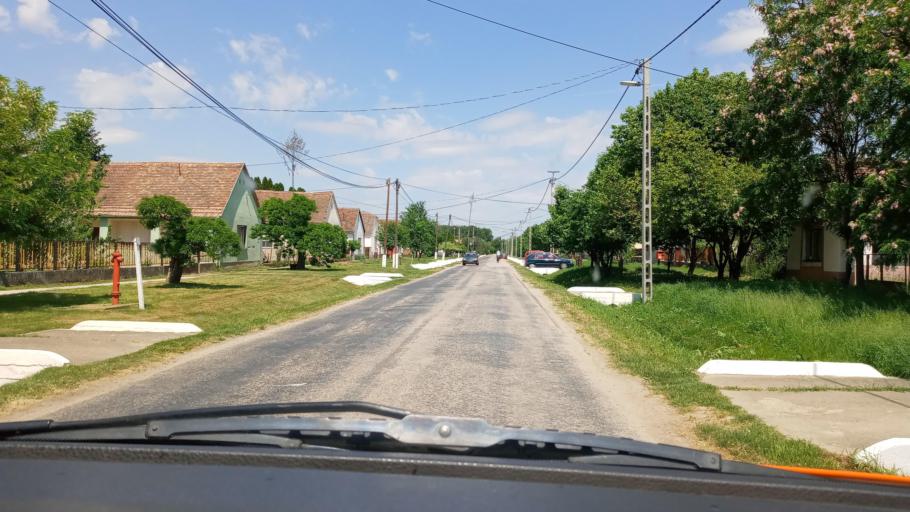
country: HR
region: Osjecko-Baranjska
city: Viljevo
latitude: 45.8126
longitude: 18.1176
